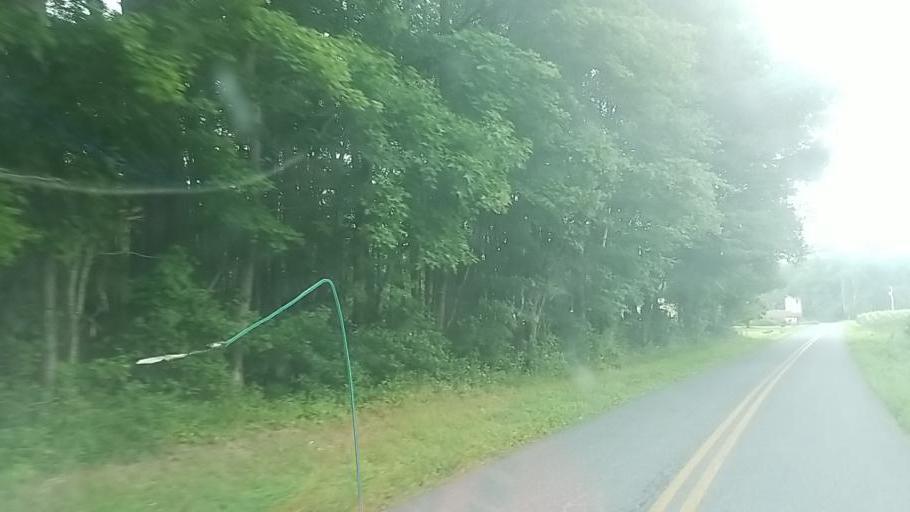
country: US
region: Maryland
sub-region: Wicomico County
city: Pittsville
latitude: 38.4293
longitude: -75.3204
